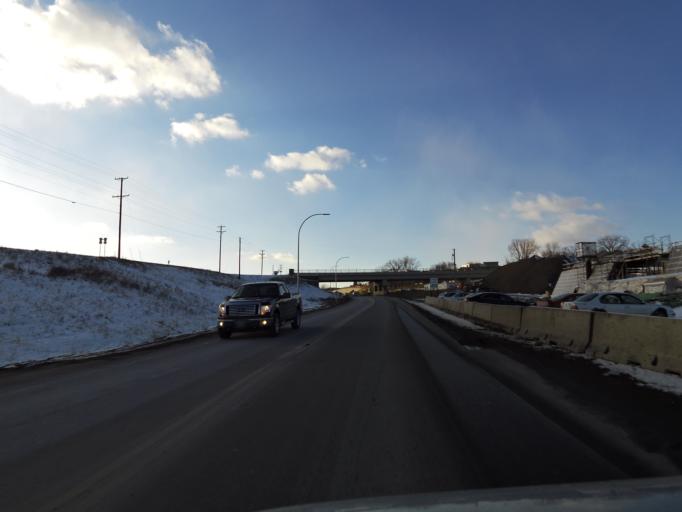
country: US
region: Minnesota
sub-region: Washington County
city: Oak Park Heights
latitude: 45.0352
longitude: -92.7950
